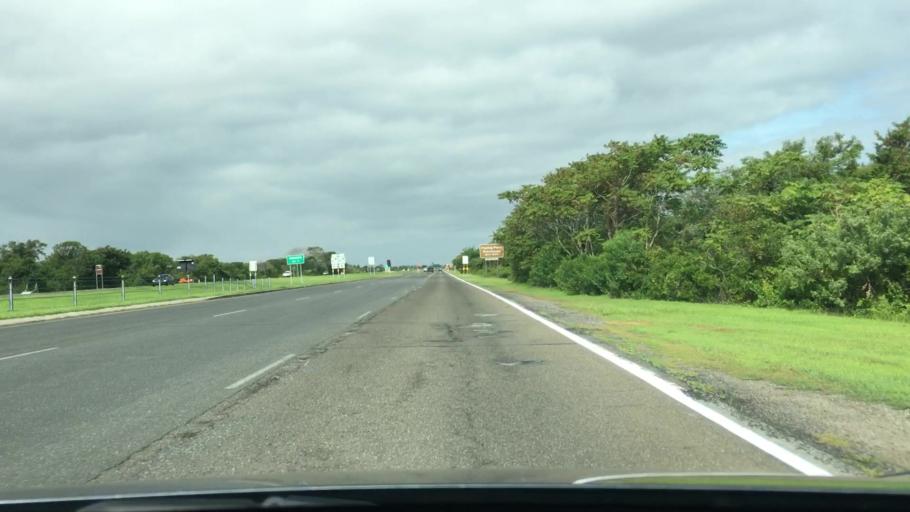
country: US
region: New York
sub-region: Nassau County
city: Point Lookout
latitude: 40.5952
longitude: -73.5219
